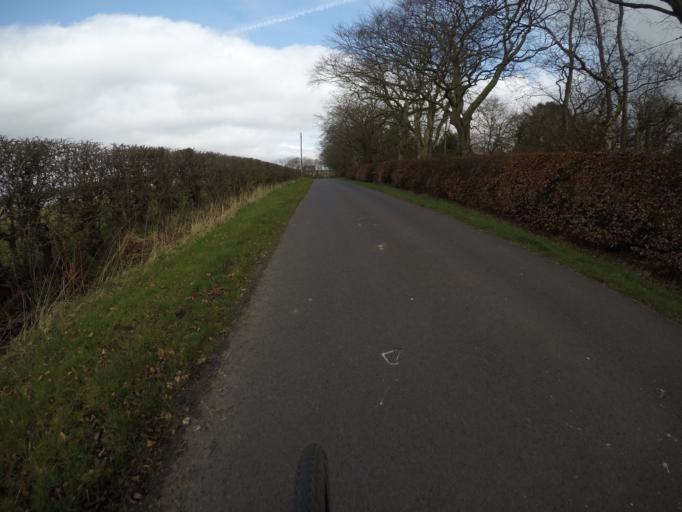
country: GB
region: Scotland
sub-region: North Ayrshire
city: Springside
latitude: 55.6578
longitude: -4.6099
